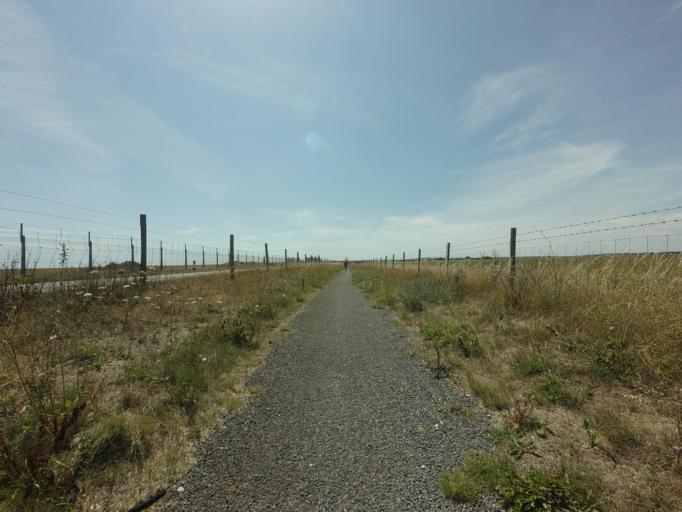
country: GB
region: England
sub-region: Kent
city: Lydd
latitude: 50.9309
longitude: 0.8378
